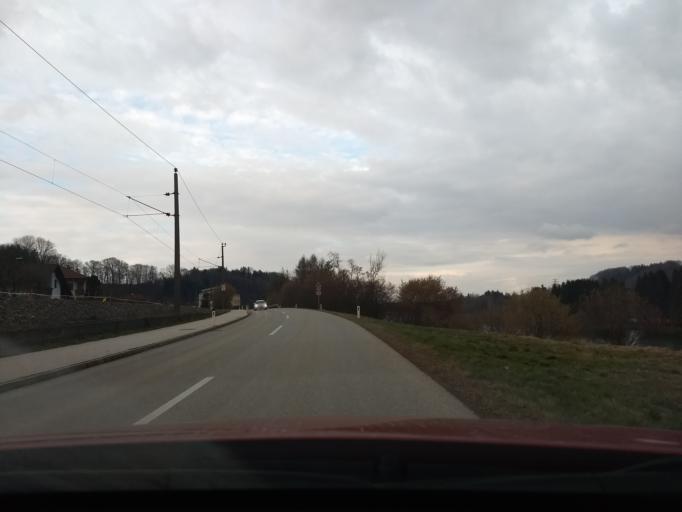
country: AT
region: Upper Austria
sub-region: Politischer Bezirk Steyr-Land
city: Garsten
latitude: 48.0054
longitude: 14.4069
